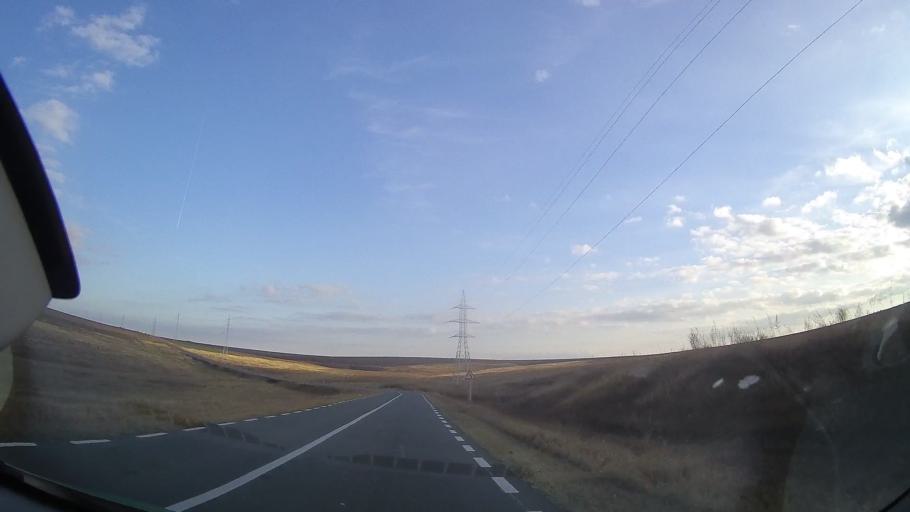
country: RO
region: Constanta
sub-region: Comuna Chirnogeni
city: Plopeni
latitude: 43.9551
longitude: 28.1502
